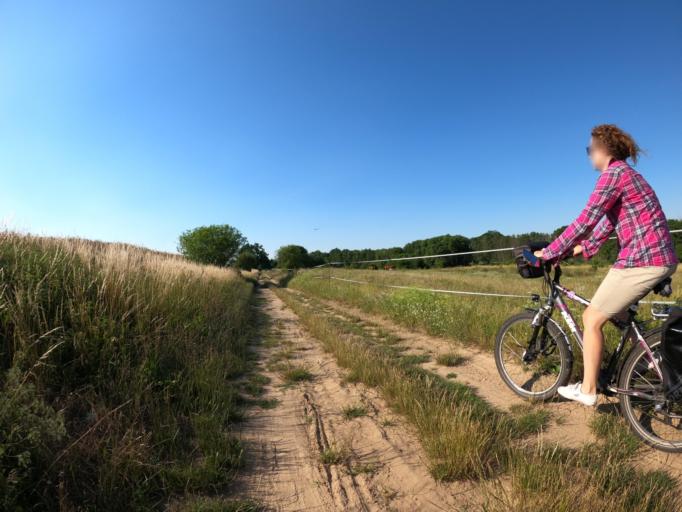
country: DE
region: Brandenburg
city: Gartz
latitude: 53.2270
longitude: 14.3692
